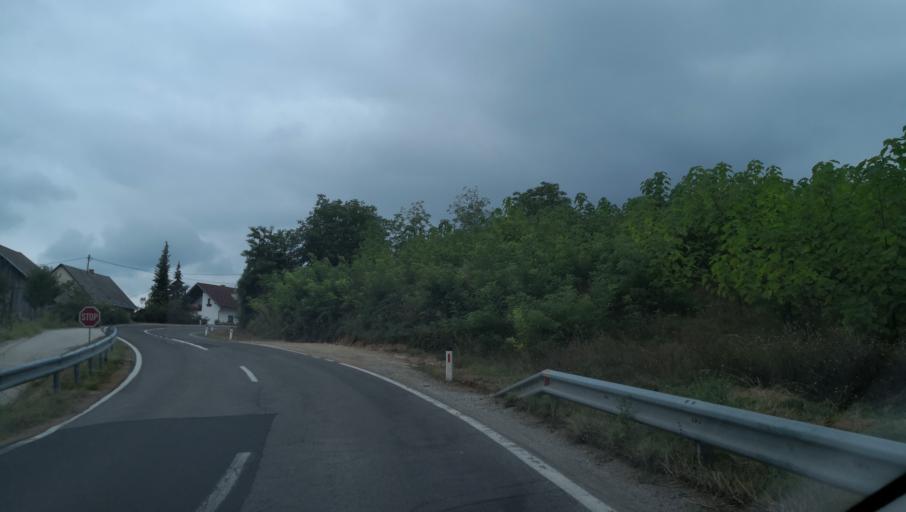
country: SI
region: Metlika
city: Metlika
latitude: 45.6915
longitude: 15.2670
